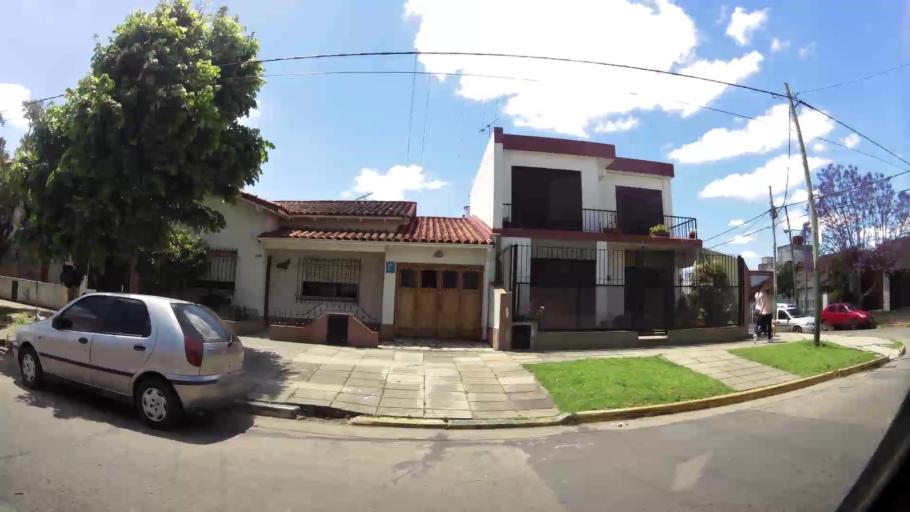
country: AR
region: Buenos Aires
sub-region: Partido de Lomas de Zamora
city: Lomas de Zamora
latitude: -34.7375
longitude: -58.4157
